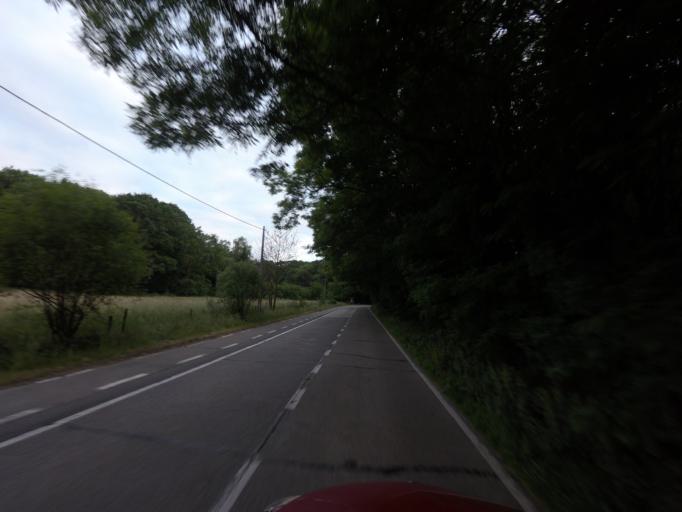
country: BE
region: Flanders
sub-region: Provincie Antwerpen
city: Herenthout
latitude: 51.1315
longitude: 4.7152
